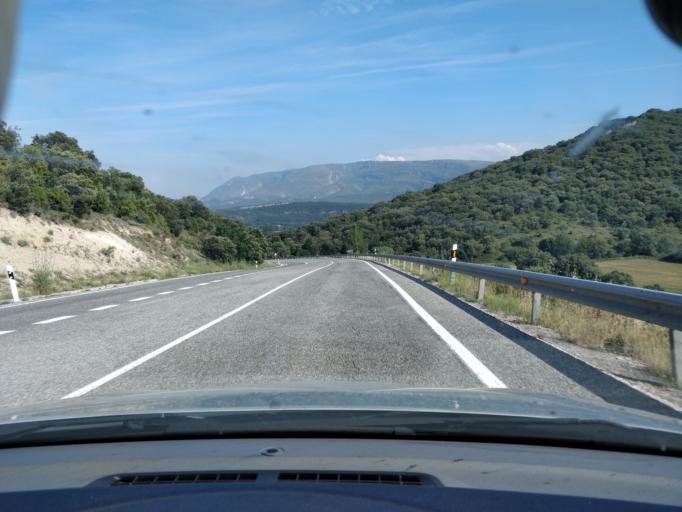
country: ES
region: Castille and Leon
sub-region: Provincia de Burgos
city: Medina de Pomar
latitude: 42.9123
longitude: -3.6067
